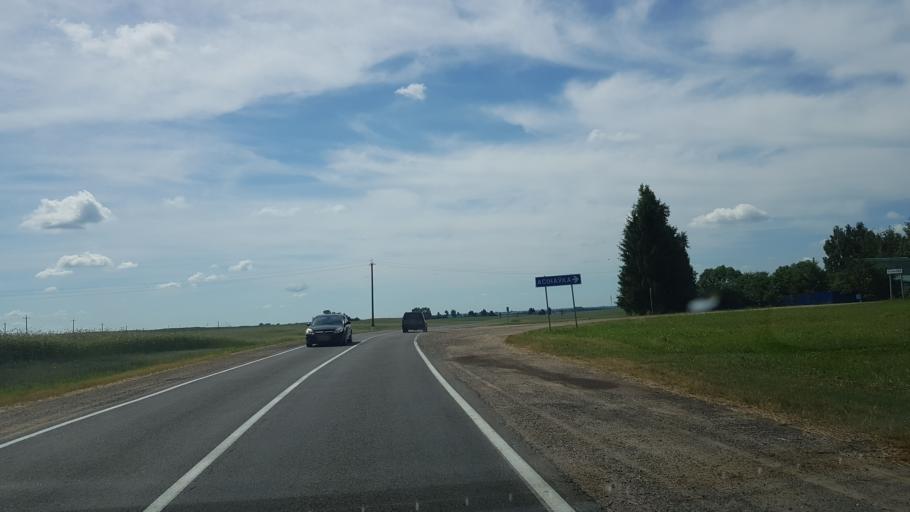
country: BY
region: Vitebsk
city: Dubrowna
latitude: 54.6512
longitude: 30.6661
